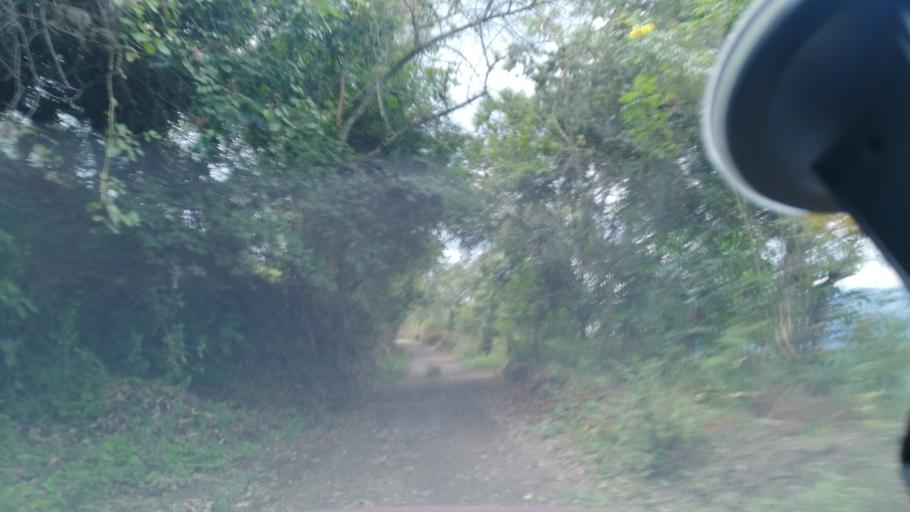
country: CO
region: Cundinamarca
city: Vergara
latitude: 5.2051
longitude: -74.2879
